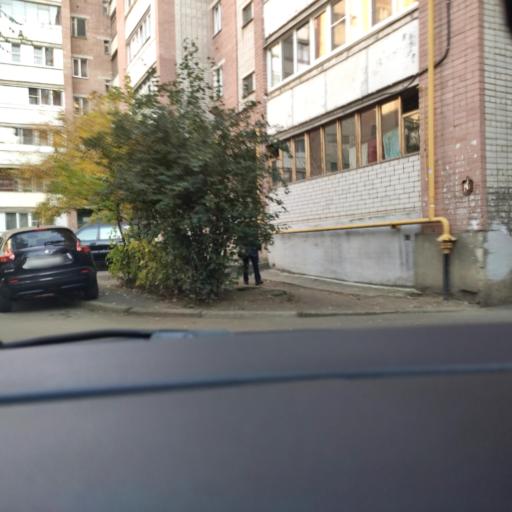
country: RU
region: Voronezj
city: Podgornoye
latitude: 51.6978
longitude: 39.1420
